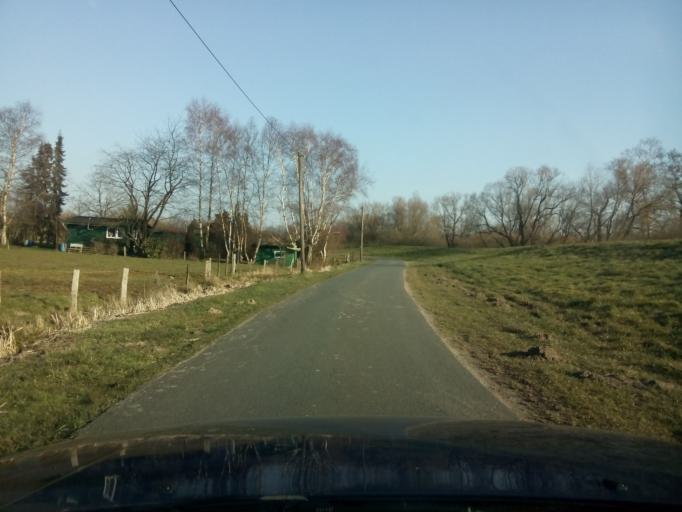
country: DE
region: Lower Saxony
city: Osterholz-Scharmbeck
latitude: 53.1625
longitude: 8.8046
